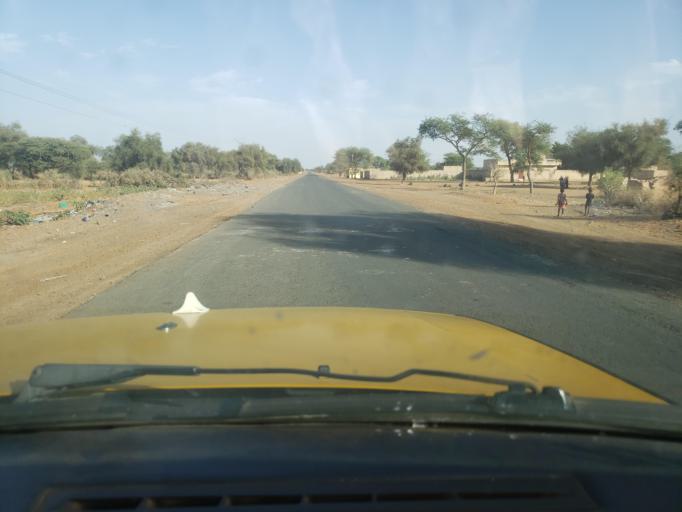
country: SN
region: Louga
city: Louga
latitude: 15.5016
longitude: -15.9412
